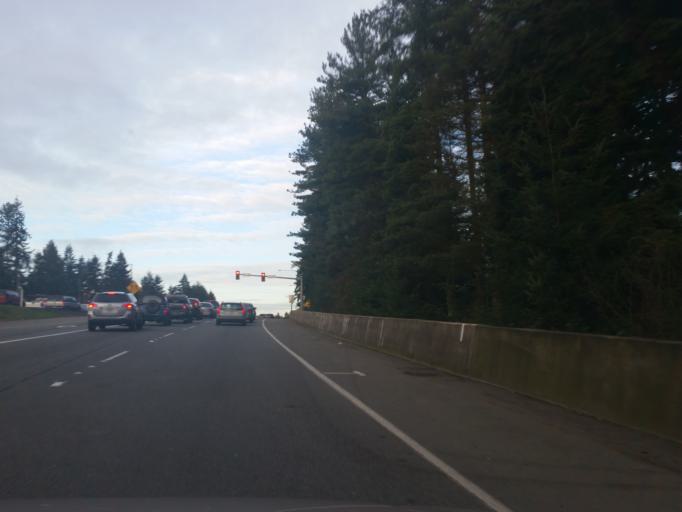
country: US
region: Washington
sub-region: King County
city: Shoreline
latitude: 47.7568
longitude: -122.3284
